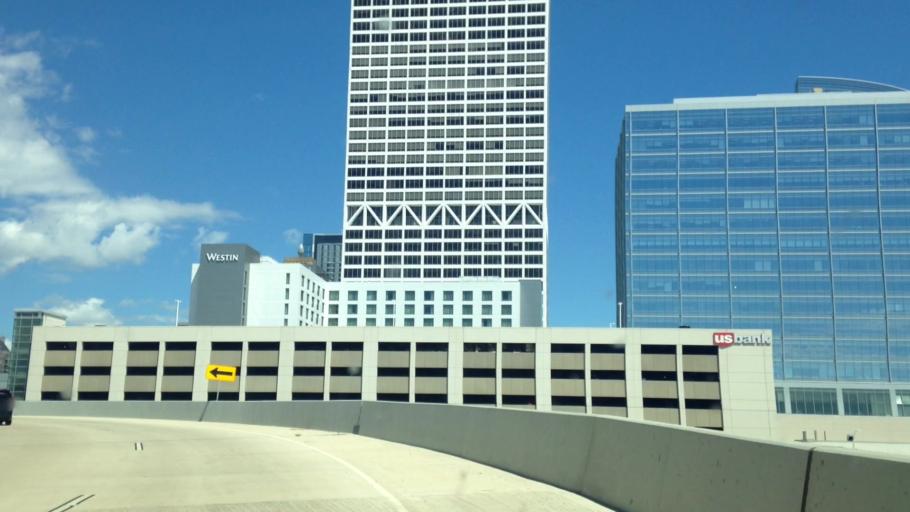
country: US
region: Wisconsin
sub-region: Milwaukee County
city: Milwaukee
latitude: 43.0356
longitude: -87.9013
